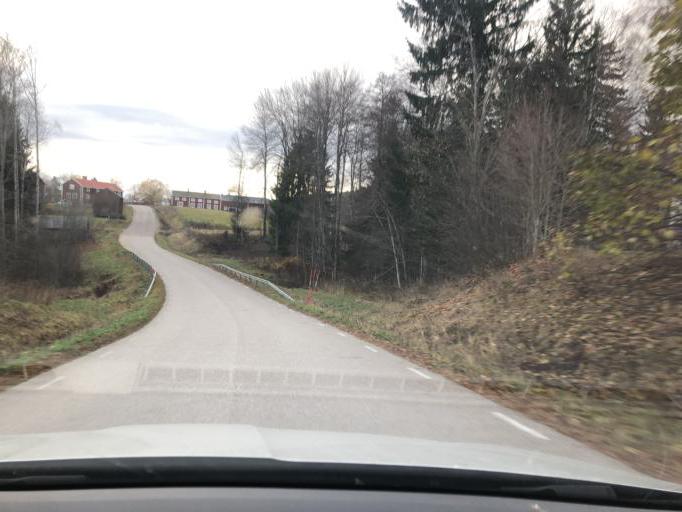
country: SE
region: Gaevleborg
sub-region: Hudiksvalls Kommun
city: Sorforsa
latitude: 61.6794
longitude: 16.9240
